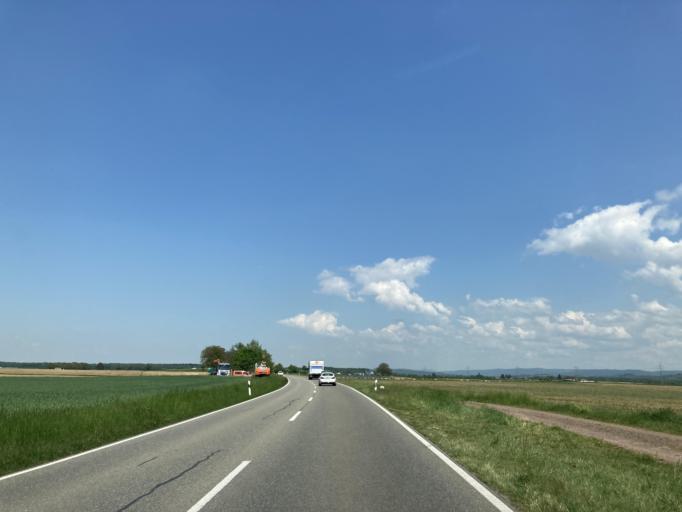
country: DE
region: Baden-Wuerttemberg
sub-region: Freiburg Region
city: Endingen
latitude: 48.1547
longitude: 7.7119
